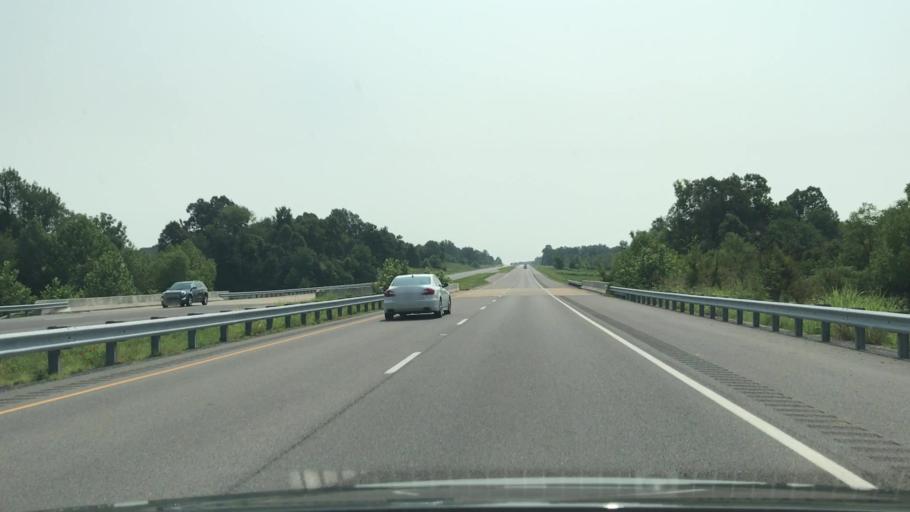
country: US
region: Kentucky
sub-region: Graves County
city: Mayfield
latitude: 36.6687
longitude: -88.4964
